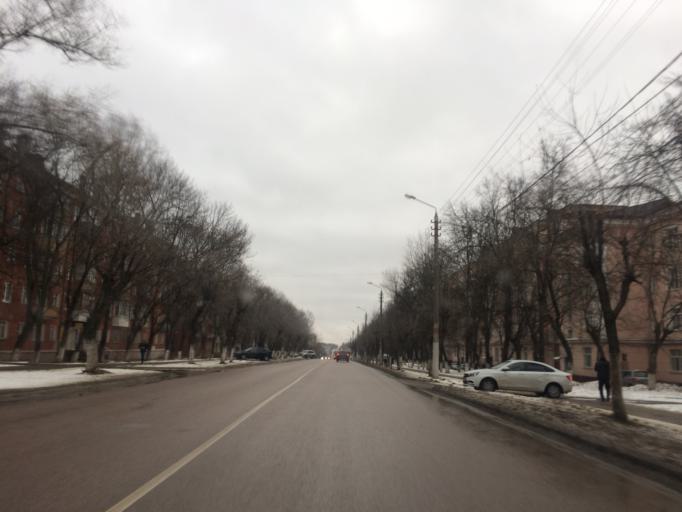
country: RU
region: Tula
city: Tula
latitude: 54.2115
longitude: 37.6676
